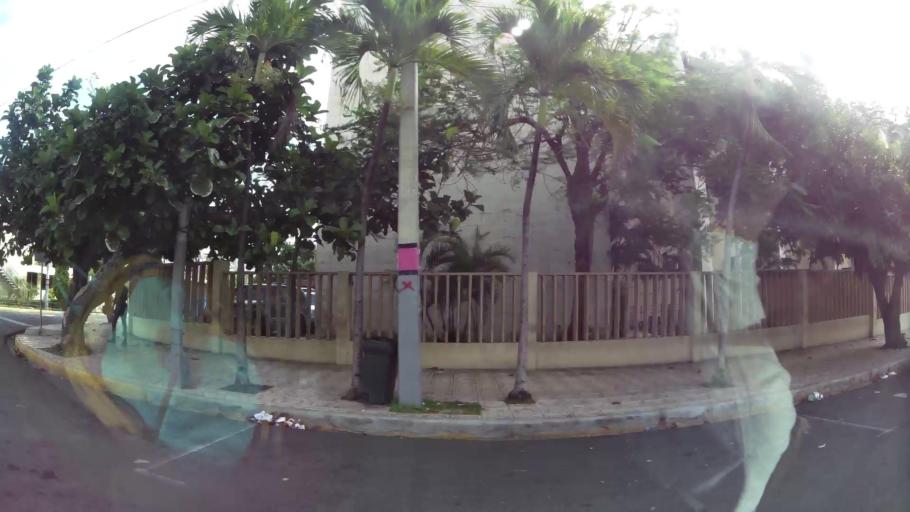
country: DO
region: Nacional
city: La Julia
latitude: 18.4493
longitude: -69.9248
